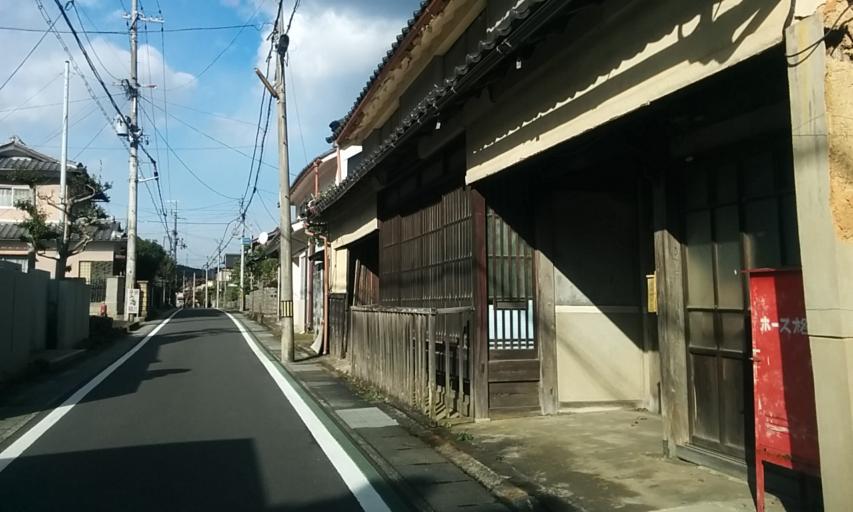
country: JP
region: Kyoto
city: Ayabe
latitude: 35.3437
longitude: 135.3101
